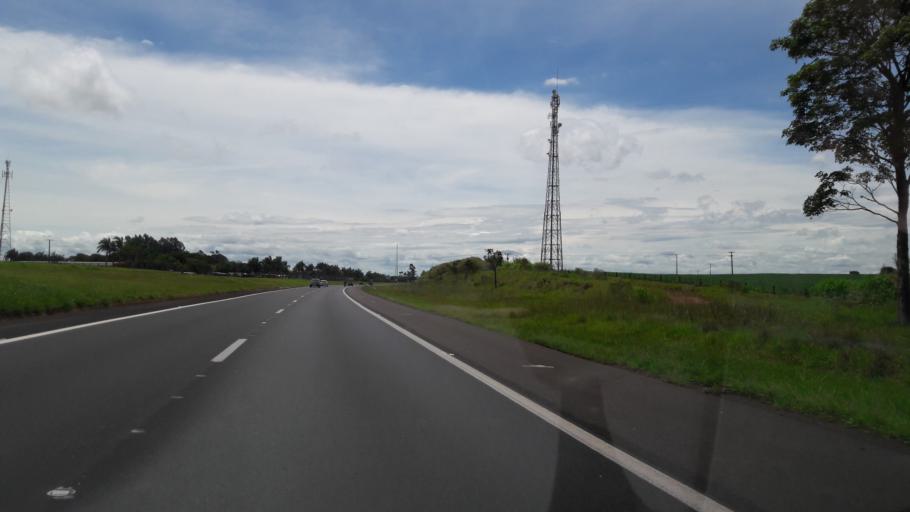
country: BR
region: Sao Paulo
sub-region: Avare
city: Avare
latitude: -22.9574
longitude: -48.8586
